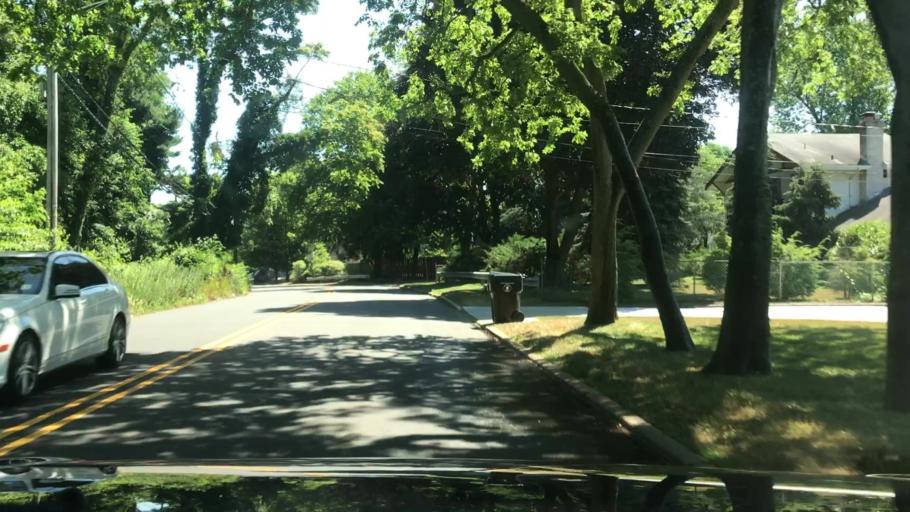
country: US
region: New Jersey
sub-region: Monmouth County
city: Red Bank
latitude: 40.3449
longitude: -74.0919
